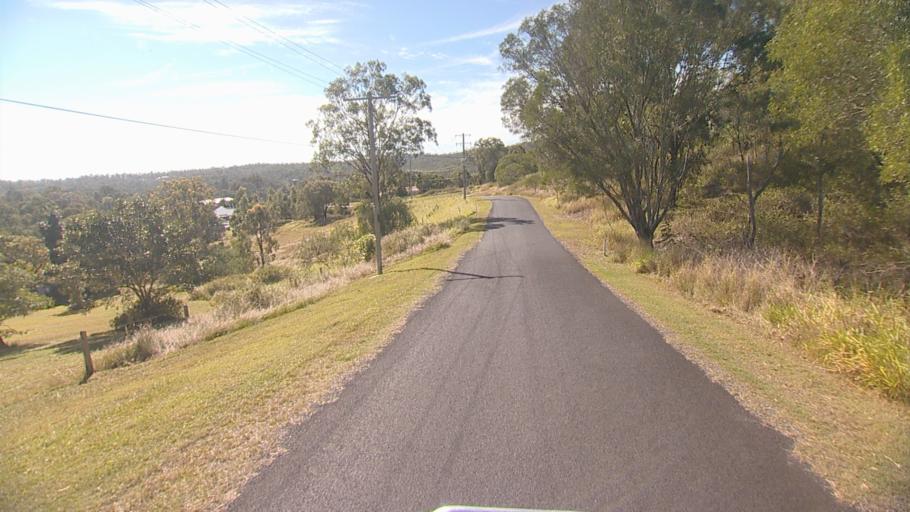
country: AU
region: Queensland
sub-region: Logan
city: Windaroo
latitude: -27.7425
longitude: 153.1724
